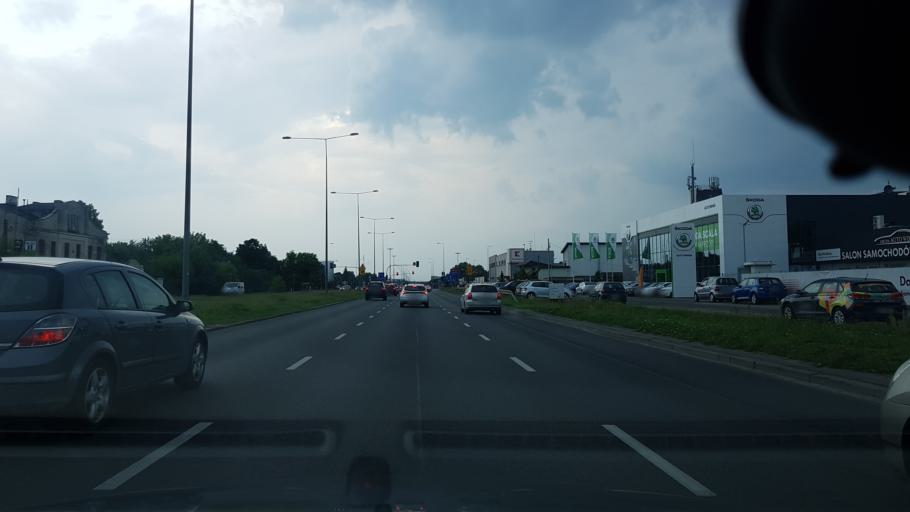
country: PL
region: Masovian Voivodeship
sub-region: Warszawa
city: Bialoleka
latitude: 52.3326
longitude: 20.9646
